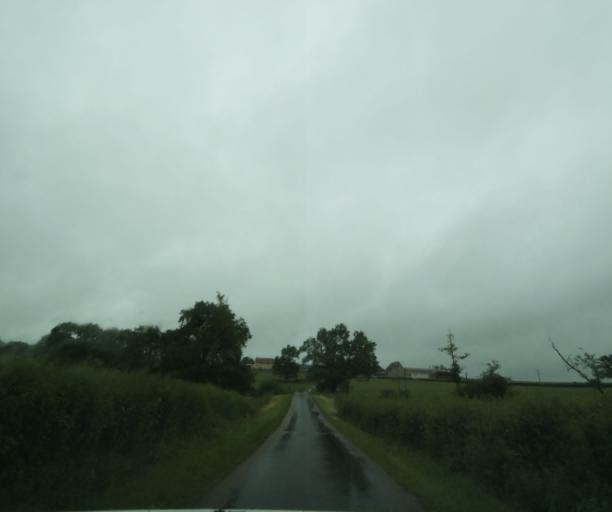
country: FR
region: Bourgogne
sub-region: Departement de Saone-et-Loire
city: Charolles
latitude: 46.4068
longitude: 4.2756
